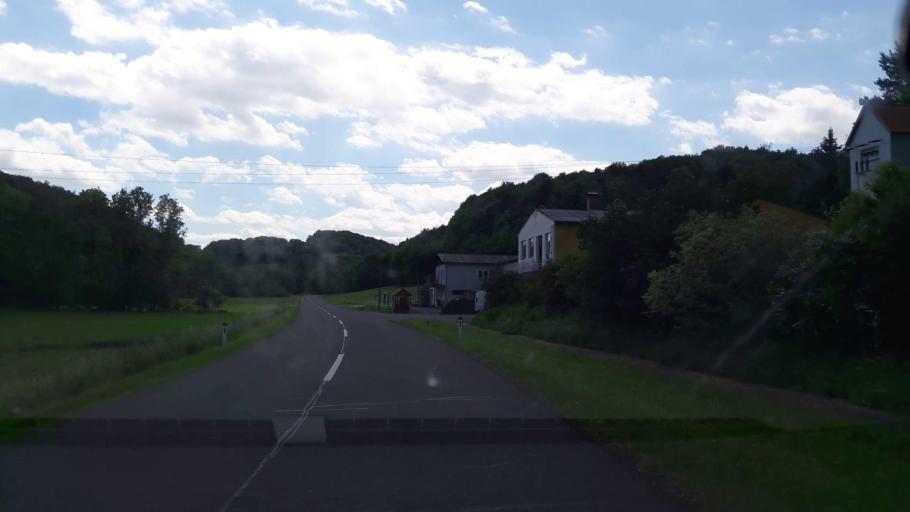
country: AT
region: Burgenland
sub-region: Politischer Bezirk Jennersdorf
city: Muhlgraben
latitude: 46.8795
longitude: 16.0596
